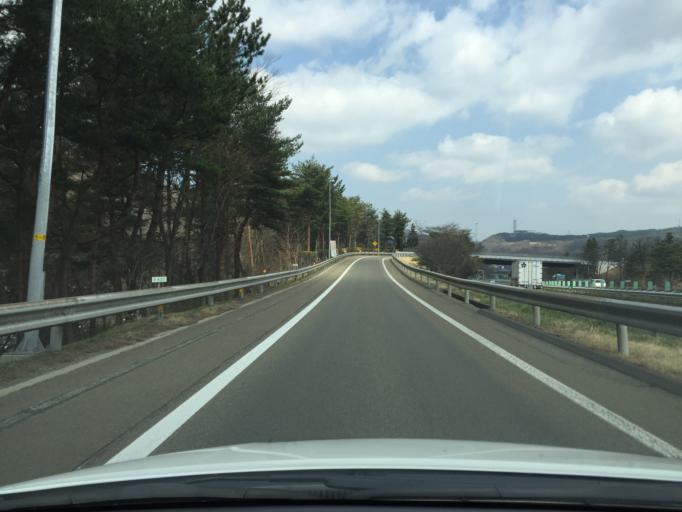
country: JP
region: Miyagi
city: Sendai
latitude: 38.2563
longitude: 140.8108
